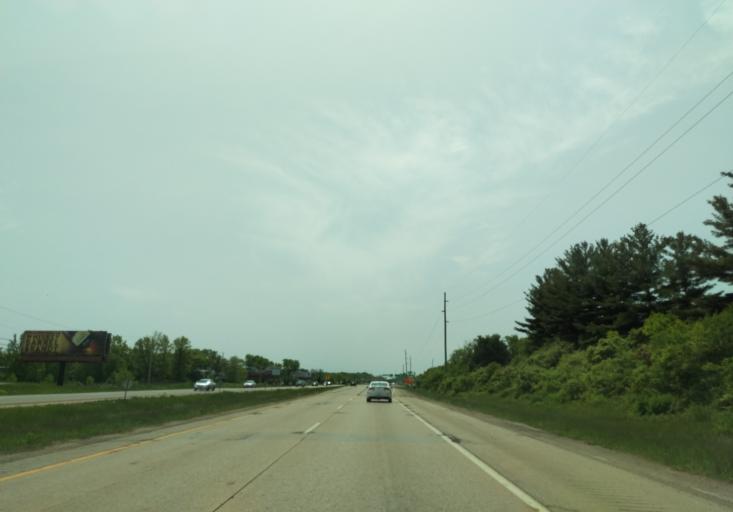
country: US
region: Wisconsin
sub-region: Dane County
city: Monona
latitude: 43.0541
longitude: -89.3090
